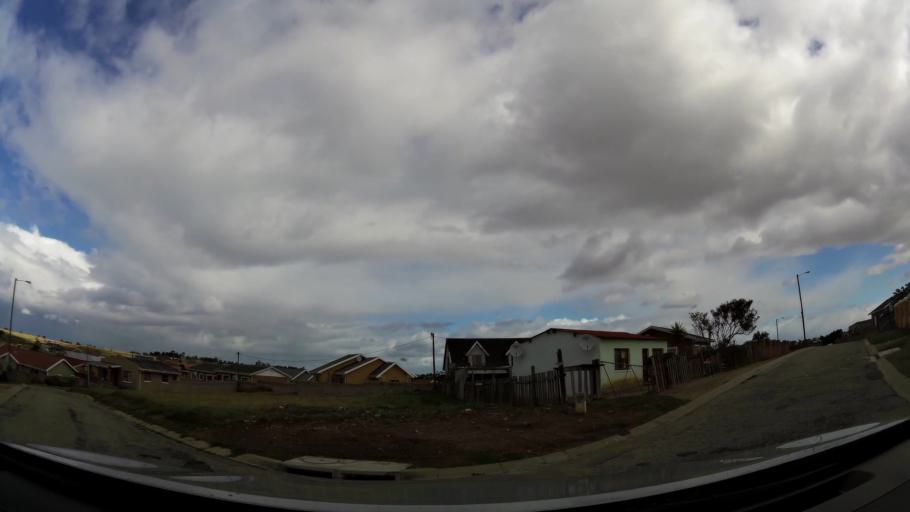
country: ZA
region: Western Cape
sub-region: Eden District Municipality
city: George
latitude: -34.0242
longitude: 22.4762
